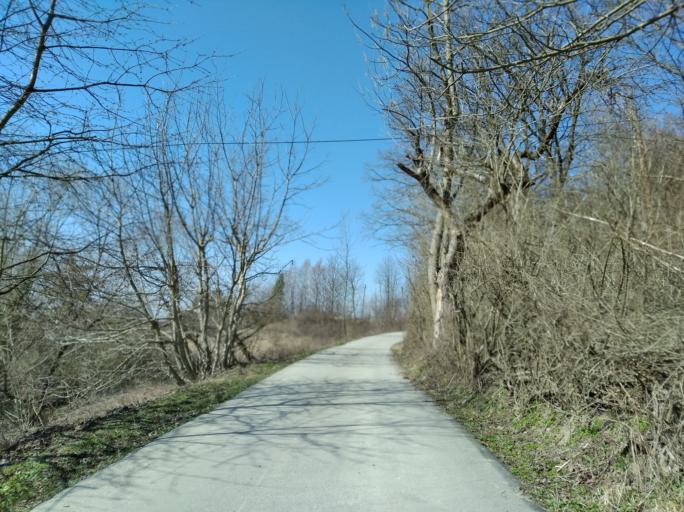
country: PL
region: Subcarpathian Voivodeship
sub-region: Powiat strzyzowski
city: Jawornik
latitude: 49.8607
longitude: 21.8509
